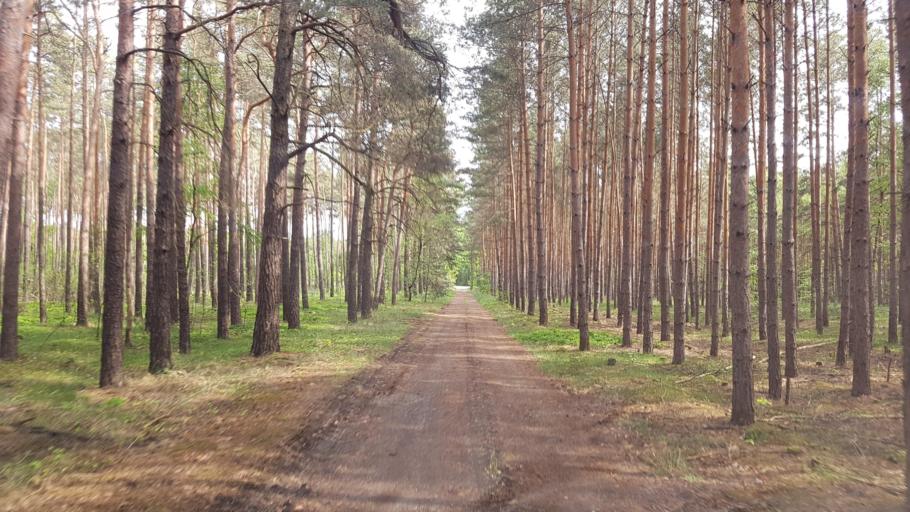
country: DE
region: Brandenburg
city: Sallgast
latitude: 51.5900
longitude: 13.8724
